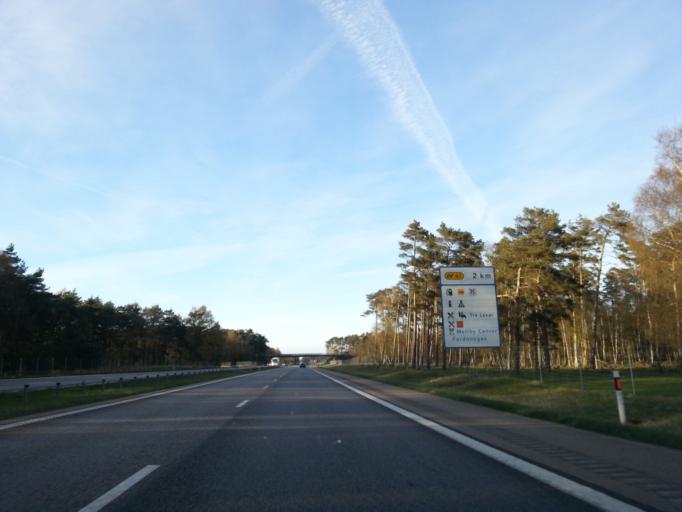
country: SE
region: Halland
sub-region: Laholms Kommun
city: Mellbystrand
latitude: 56.4818
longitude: 12.9475
